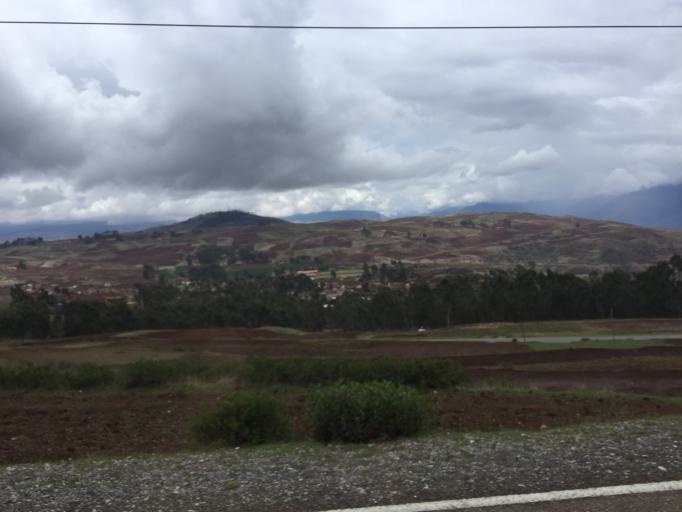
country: PE
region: Cusco
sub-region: Provincia de Urubamba
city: Huayllabamba
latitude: -13.3670
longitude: -72.0688
